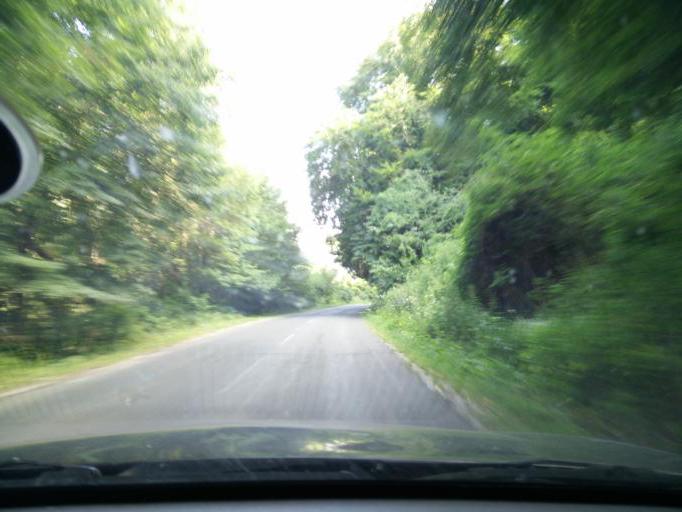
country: HU
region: Komarom-Esztergom
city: Tardos
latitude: 47.6696
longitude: 18.4435
